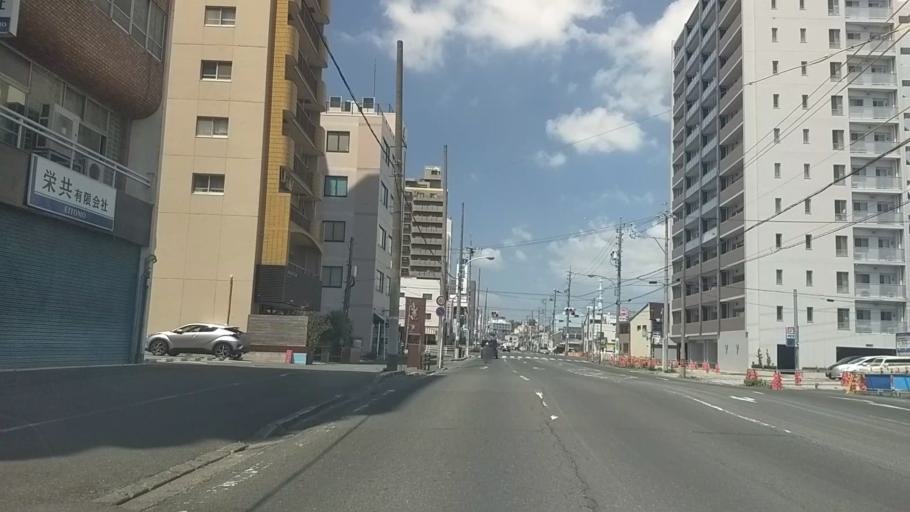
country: JP
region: Shizuoka
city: Hamamatsu
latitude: 34.7139
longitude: 137.7319
